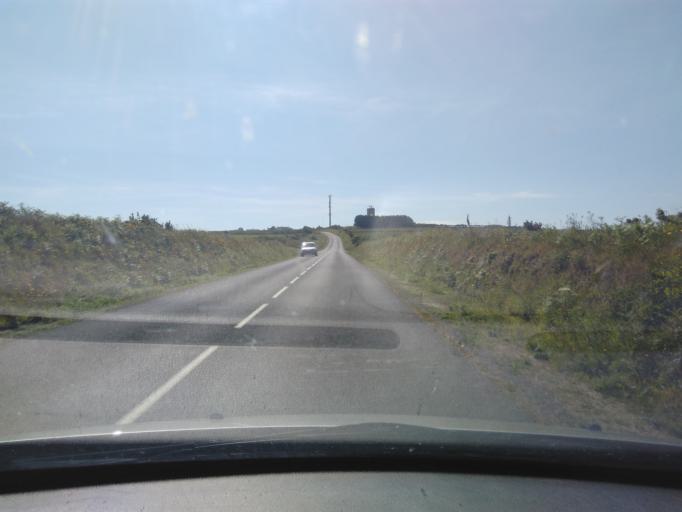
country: FR
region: Lower Normandy
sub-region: Departement de la Manche
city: Beaumont-Hague
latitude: 49.6889
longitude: -1.9132
